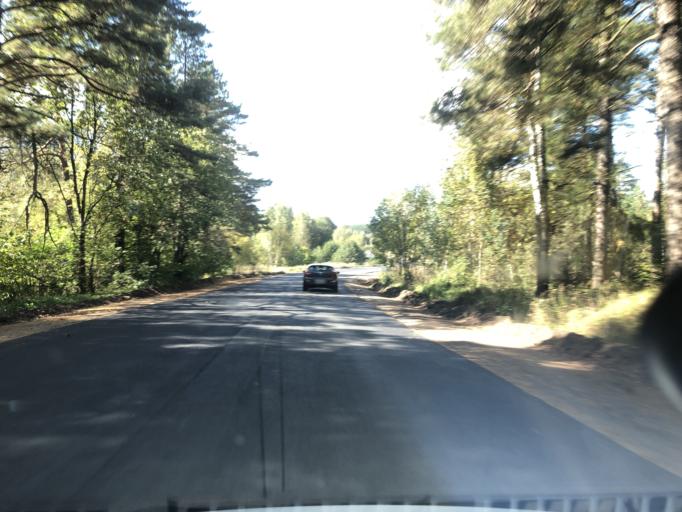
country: RU
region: Jaroslavl
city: Porech'ye-Rybnoye
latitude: 56.9714
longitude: 39.4183
